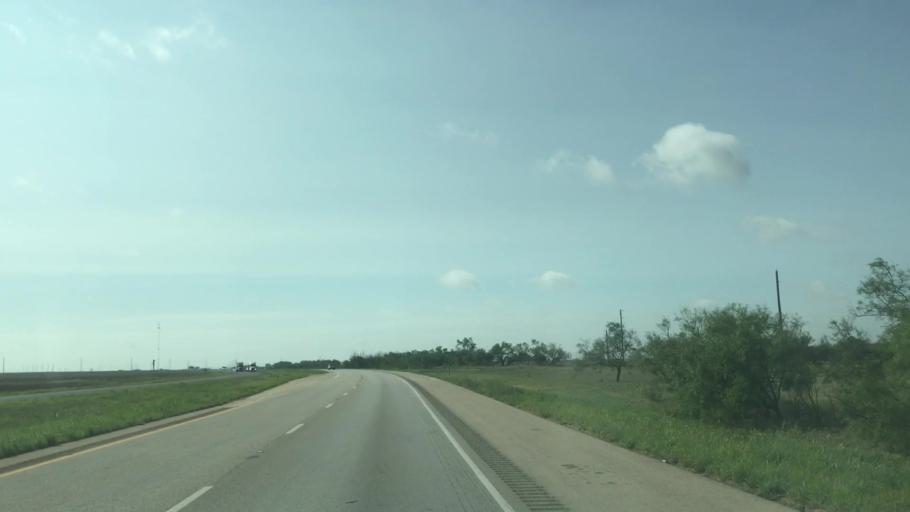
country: US
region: Texas
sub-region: Nolan County
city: Roscoe
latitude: 32.5764
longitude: -100.7219
